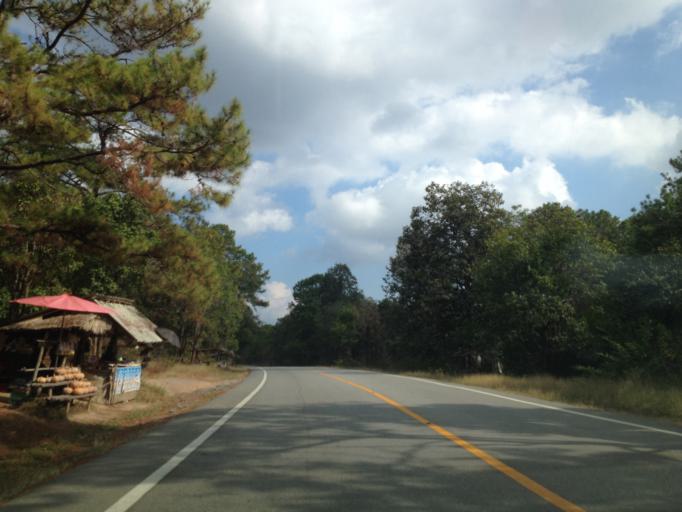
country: TH
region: Chiang Mai
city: Hot
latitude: 18.1469
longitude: 98.3831
